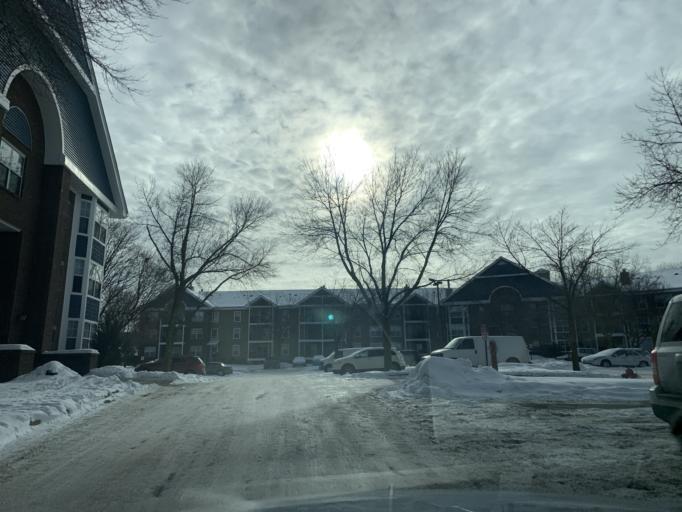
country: US
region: Minnesota
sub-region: Dakota County
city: Burnsville
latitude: 44.7517
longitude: -93.2789
